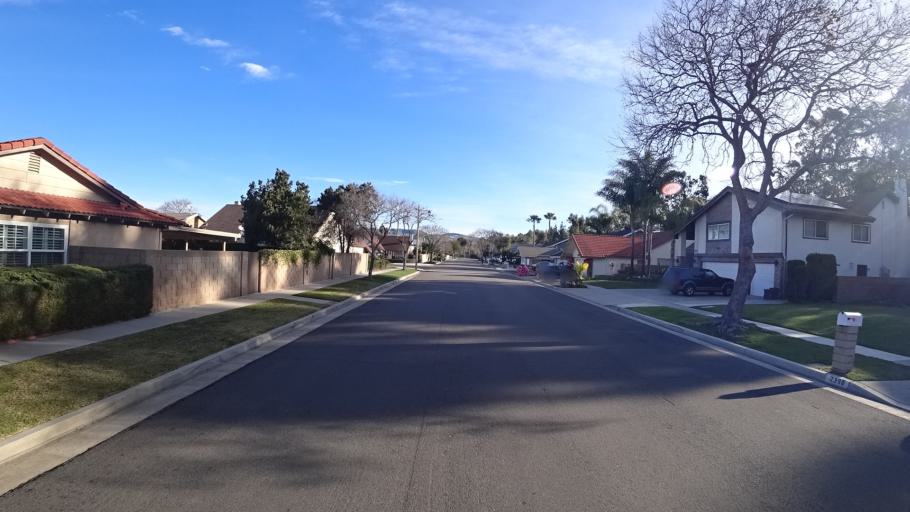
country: US
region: California
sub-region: Orange County
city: Yorba Linda
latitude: 33.8597
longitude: -117.7692
